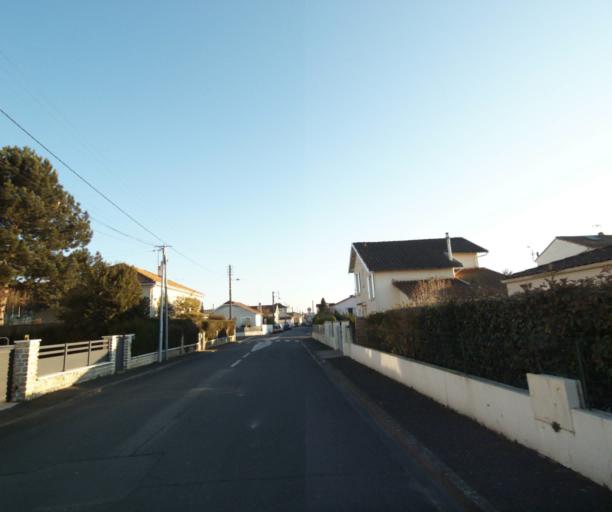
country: FR
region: Poitou-Charentes
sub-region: Departement des Deux-Sevres
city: Niort
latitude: 46.3312
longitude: -0.4740
